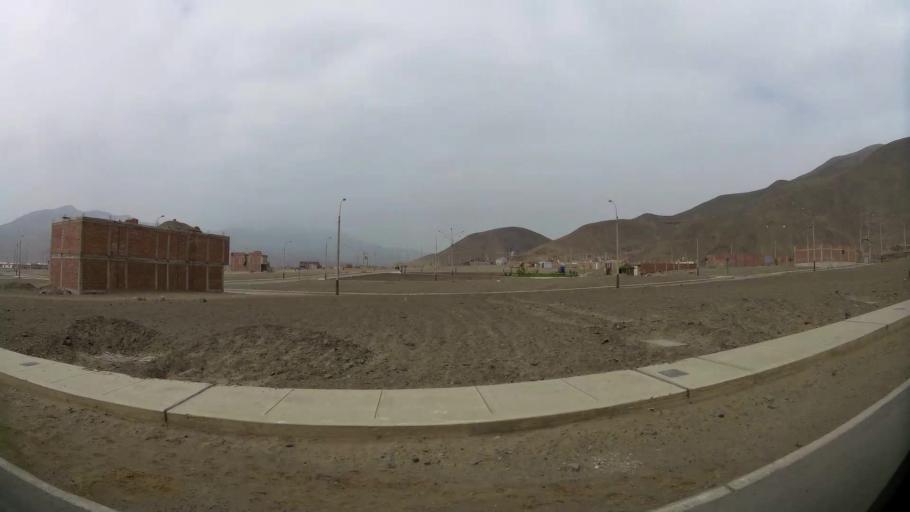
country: PE
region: Lima
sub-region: Lima
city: Santa Rosa
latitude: -11.7931
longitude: -77.1522
